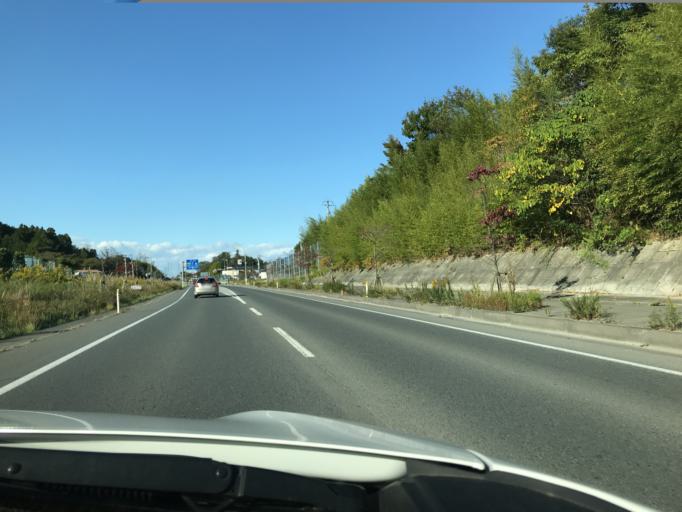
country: JP
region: Miyagi
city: Marumori
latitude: 37.8161
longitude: 140.9431
